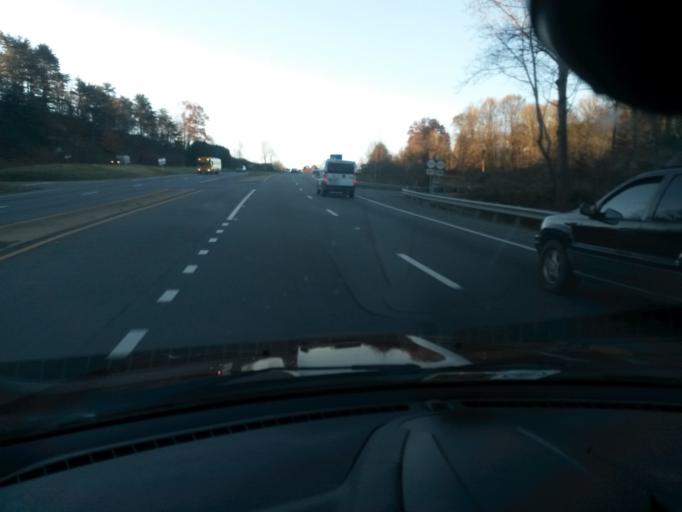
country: US
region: Virginia
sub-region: Franklin County
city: Rocky Mount
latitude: 37.0289
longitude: -79.8796
